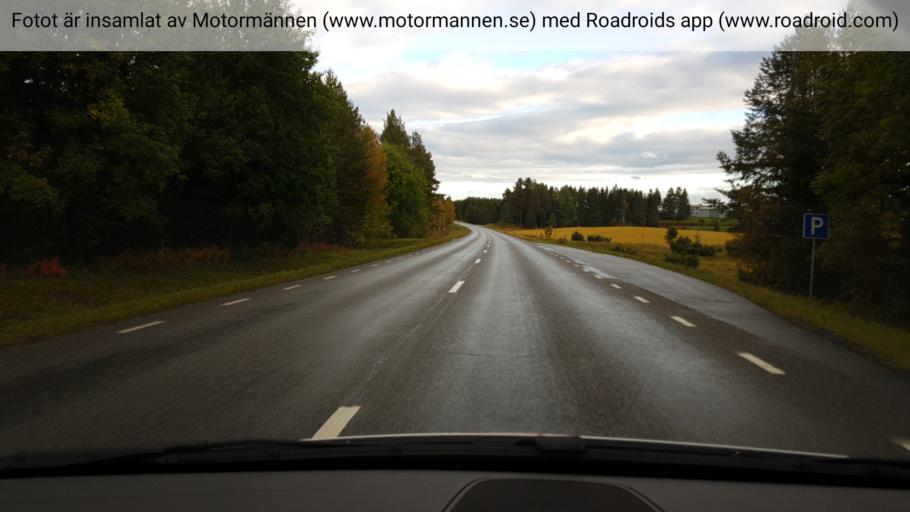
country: SE
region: Jaemtland
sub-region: Krokoms Kommun
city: Valla
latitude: 63.2780
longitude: 13.9372
